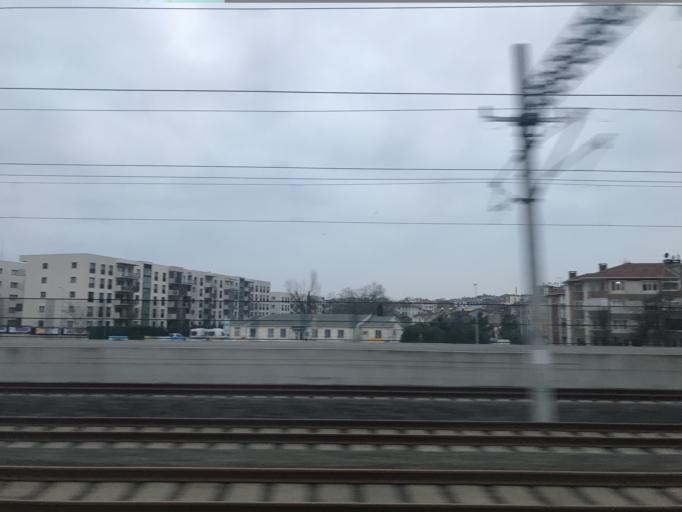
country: TR
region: Istanbul
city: Icmeler
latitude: 40.8332
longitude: 29.3171
